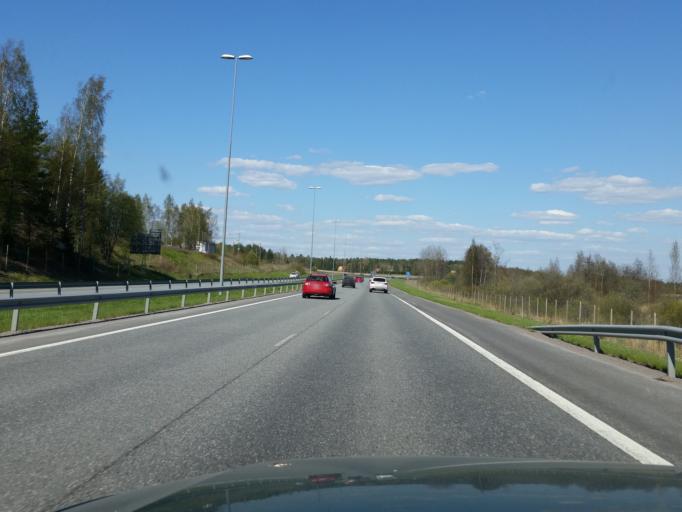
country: FI
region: Uusimaa
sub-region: Helsinki
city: Kirkkonummi
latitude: 60.1253
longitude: 24.4900
